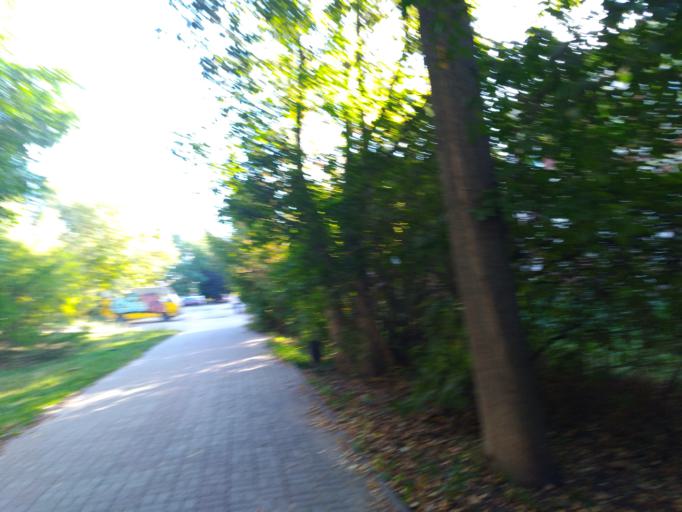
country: RU
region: Kaluga
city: Kaluga
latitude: 54.5309
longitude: 36.2752
